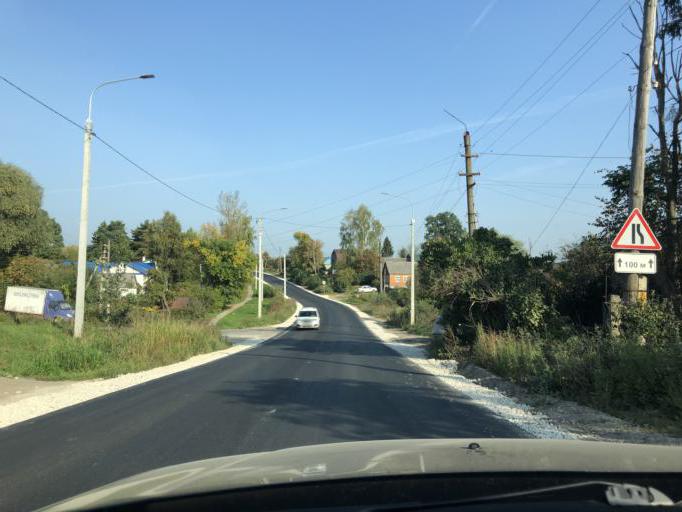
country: RU
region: Tula
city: Leninskiy
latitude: 54.2929
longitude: 37.4635
